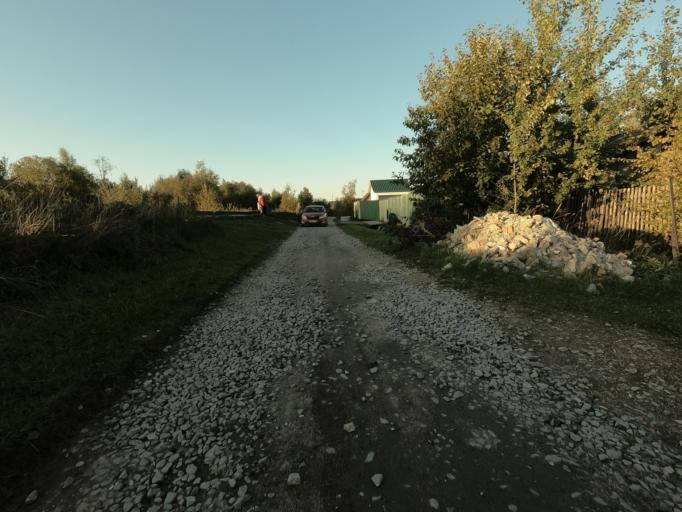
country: RU
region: Leningrad
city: Nikol'skoye
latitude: 59.7063
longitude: 30.7970
